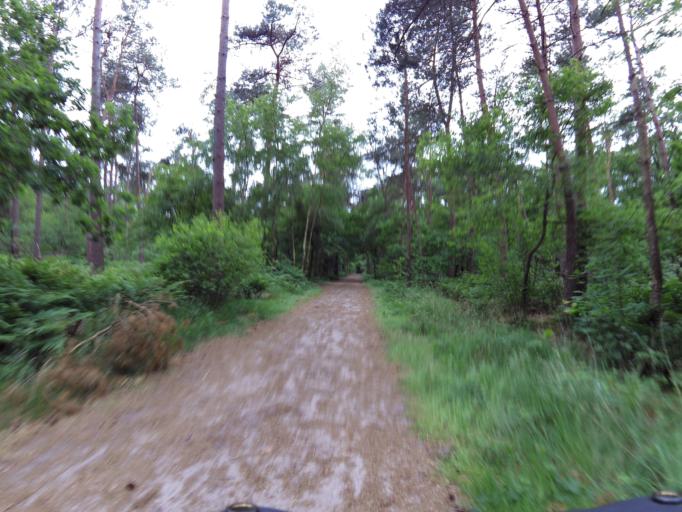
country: NL
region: North Brabant
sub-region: Gemeente Breda
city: Breda
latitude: 51.5585
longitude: 4.7719
